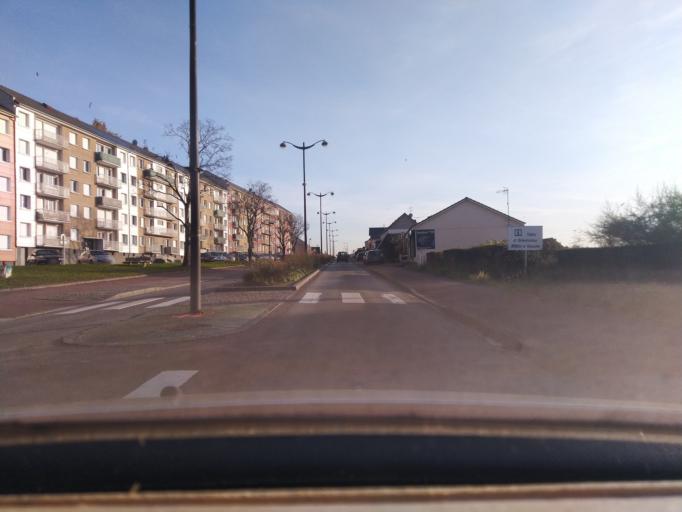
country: FR
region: Haute-Normandie
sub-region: Departement de la Seine-Maritime
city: Le Trait
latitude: 49.4753
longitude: 0.8133
